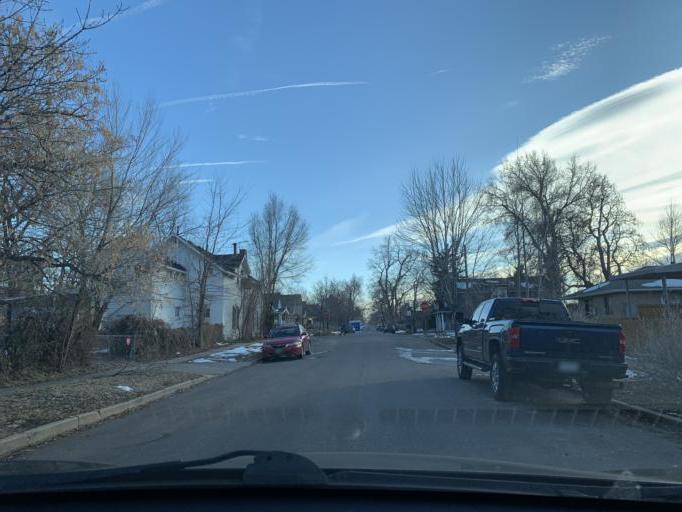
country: US
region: Colorado
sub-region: Jefferson County
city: Edgewater
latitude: 39.7718
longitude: -105.0382
